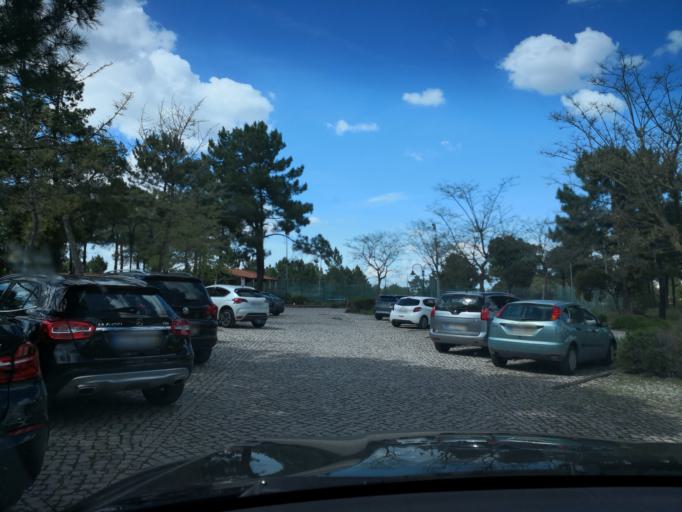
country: PT
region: Setubal
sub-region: Seixal
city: Aldeia de Paio Pires
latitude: 38.5442
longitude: -9.0534
